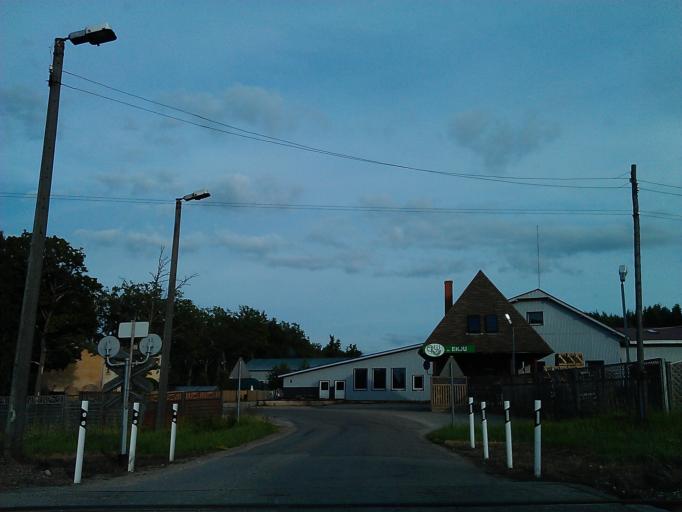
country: LV
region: Amatas Novads
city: Drabesi
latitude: 57.2012
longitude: 25.1755
